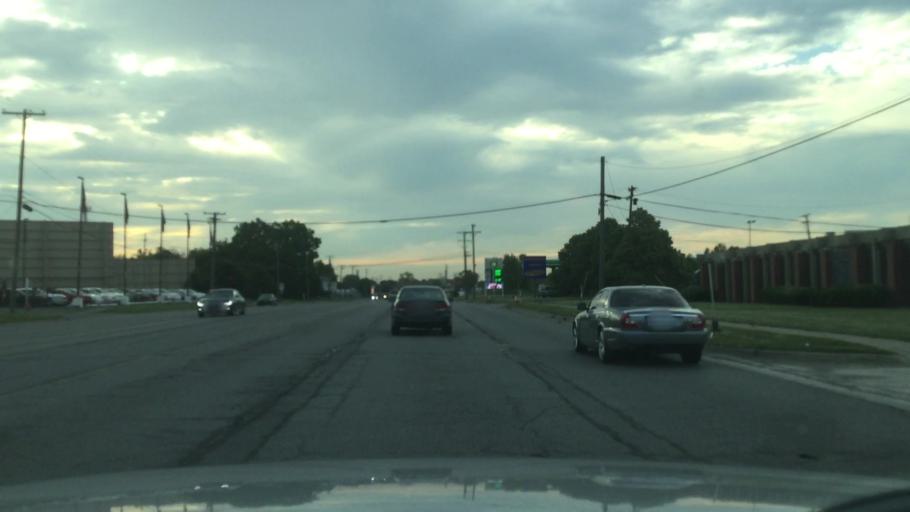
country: US
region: Michigan
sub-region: Wayne County
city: Dearborn
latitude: 42.3297
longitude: -83.1642
